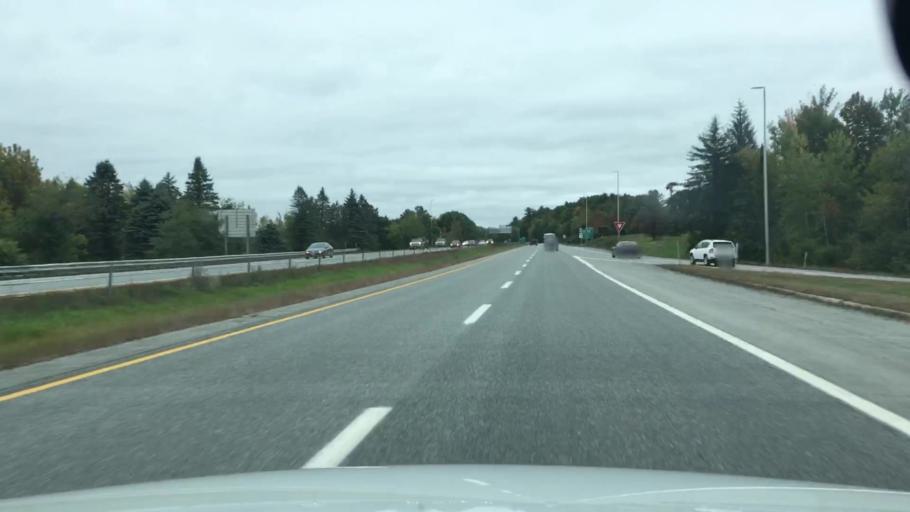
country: US
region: Maine
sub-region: Penobscot County
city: Bangor
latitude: 44.7896
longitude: -68.8064
